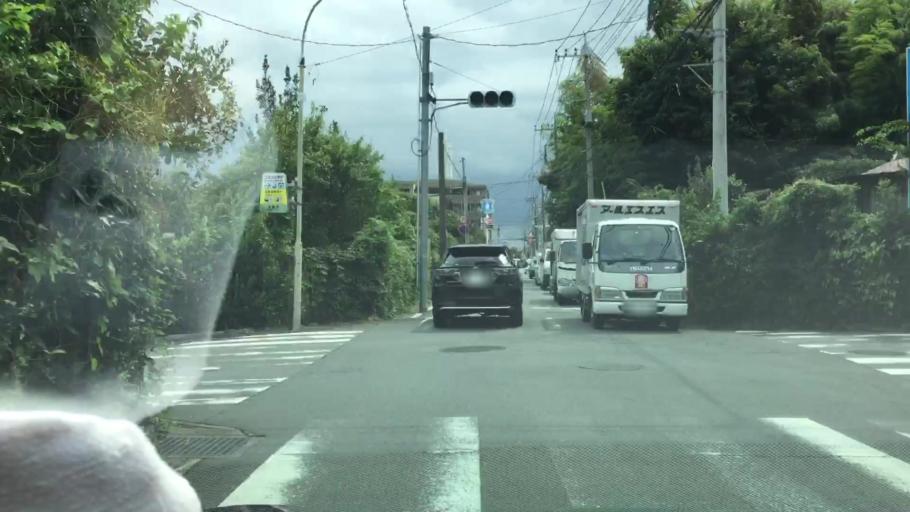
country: JP
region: Saitama
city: Ageoshimo
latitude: 35.9386
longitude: 139.6061
